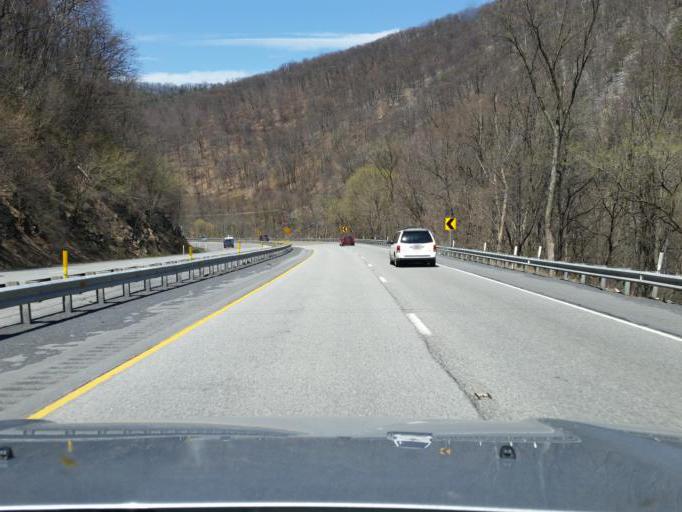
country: US
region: Pennsylvania
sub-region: Mifflin County
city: Yeagertown
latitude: 40.6517
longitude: -77.5830
